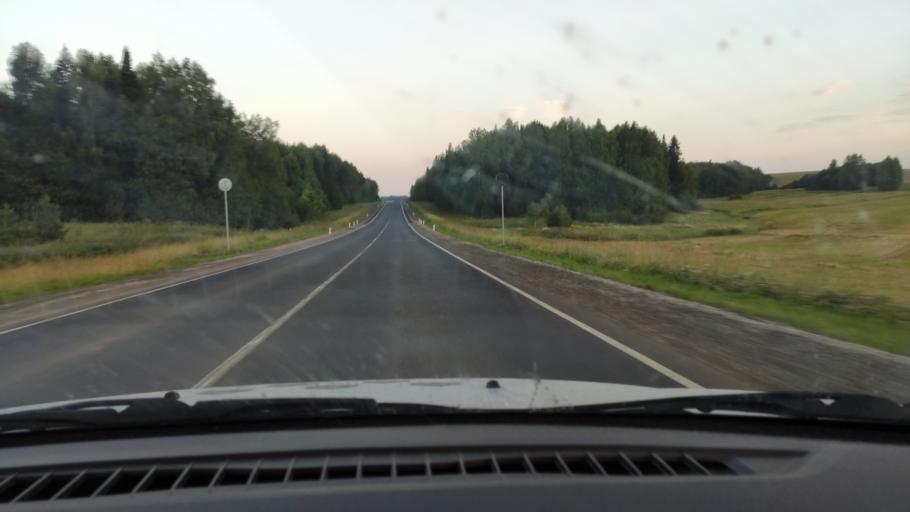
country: RU
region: Perm
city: Siva
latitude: 58.4003
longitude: 54.4965
